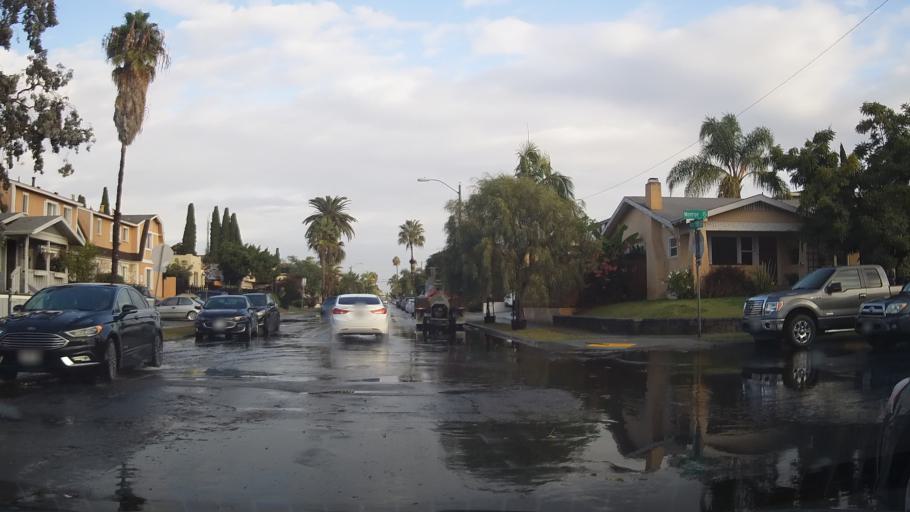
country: US
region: California
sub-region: San Diego County
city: San Diego
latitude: 32.7590
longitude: -117.1240
